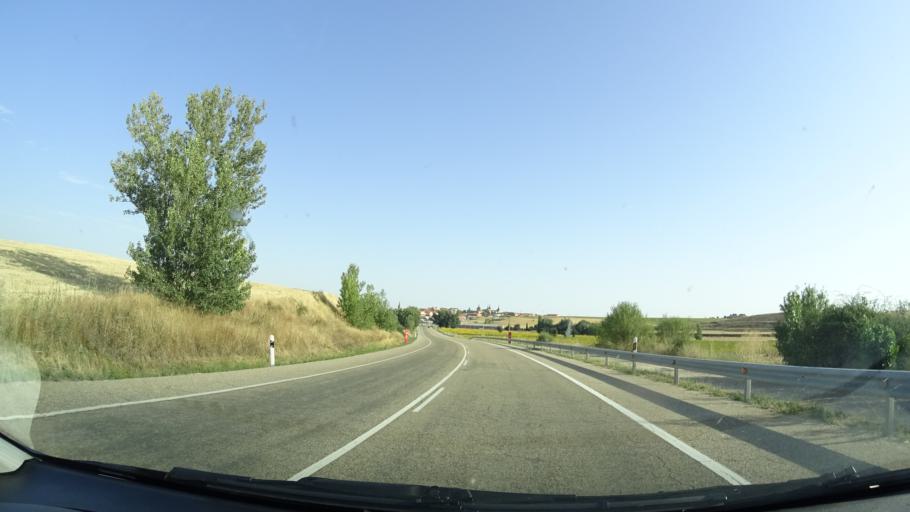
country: ES
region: Castille and Leon
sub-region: Provincia de Burgos
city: Lerma
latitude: 42.0135
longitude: -3.7516
